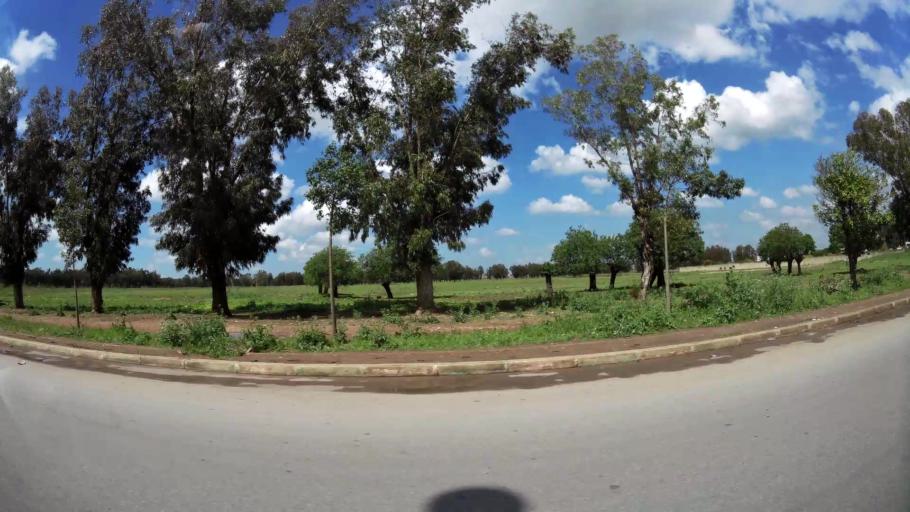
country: MA
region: Chaouia-Ouardigha
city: Nouaseur
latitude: 33.3734
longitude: -7.5516
